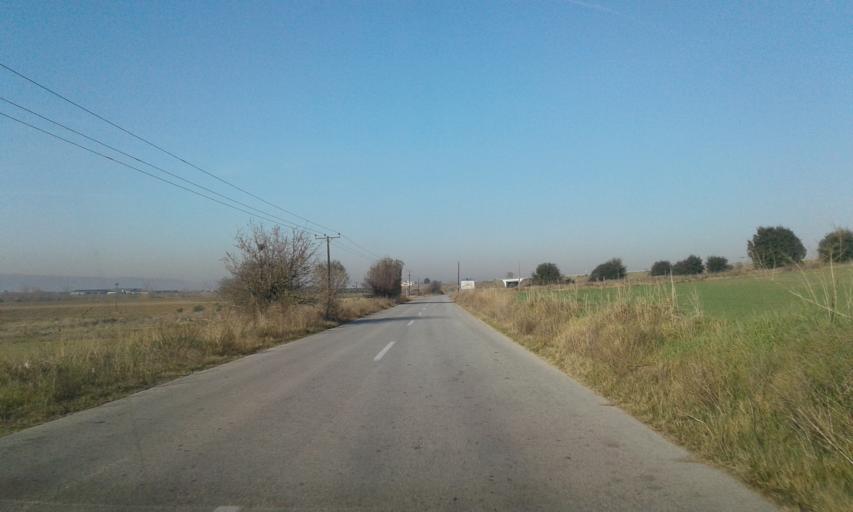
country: GR
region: Central Macedonia
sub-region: Nomos Thessalonikis
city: Kolchikon
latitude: 40.7072
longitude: 23.1874
